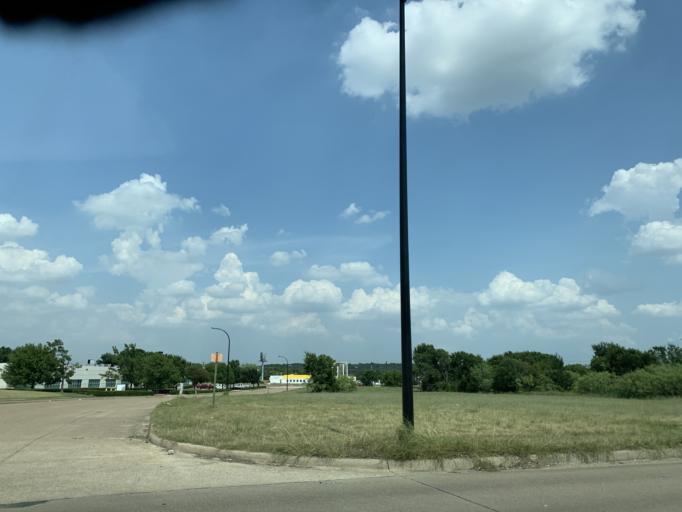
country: US
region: Texas
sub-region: Tarrant County
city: Richland Hills
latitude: 32.7753
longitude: -97.2157
